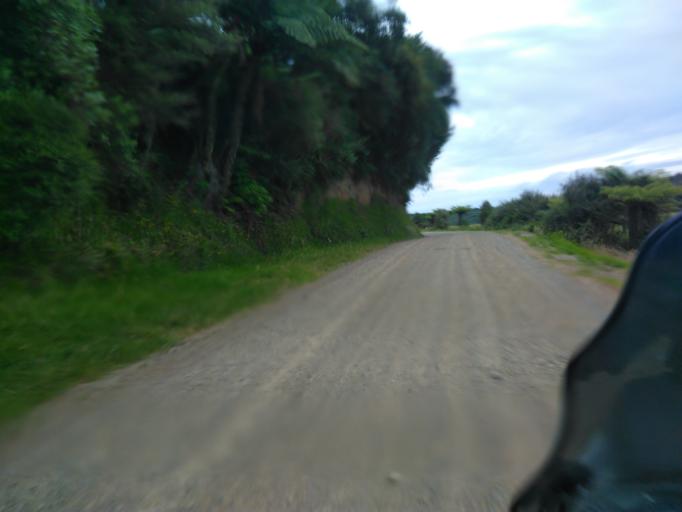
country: NZ
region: Bay of Plenty
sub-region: Opotiki District
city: Opotiki
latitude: -38.0212
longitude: 177.4349
